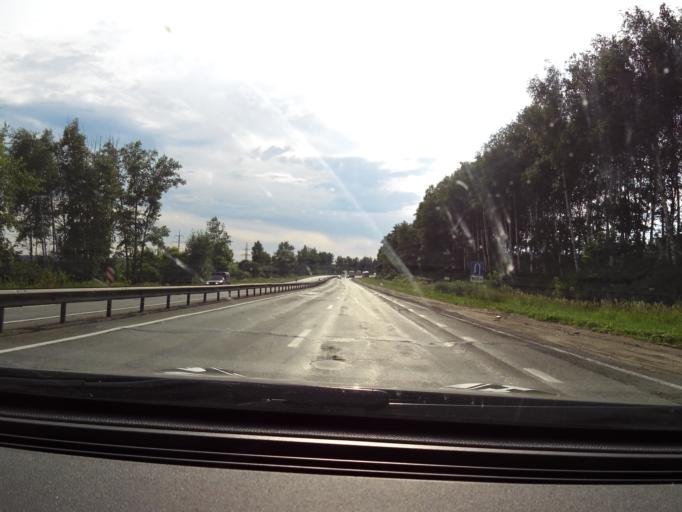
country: RU
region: Vladimir
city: Gorokhovets
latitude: 56.1591
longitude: 42.5248
